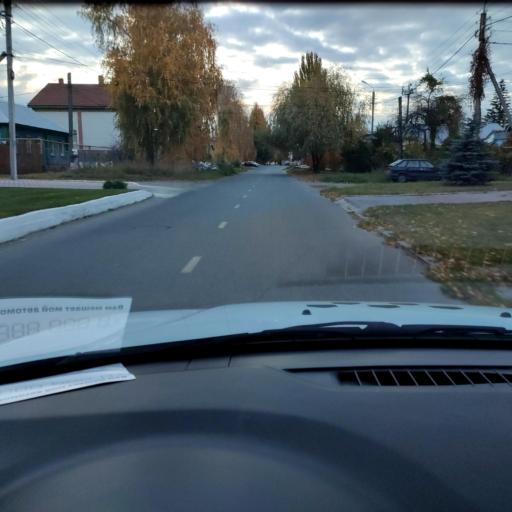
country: RU
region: Samara
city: Tol'yatti
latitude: 53.5178
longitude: 49.3985
